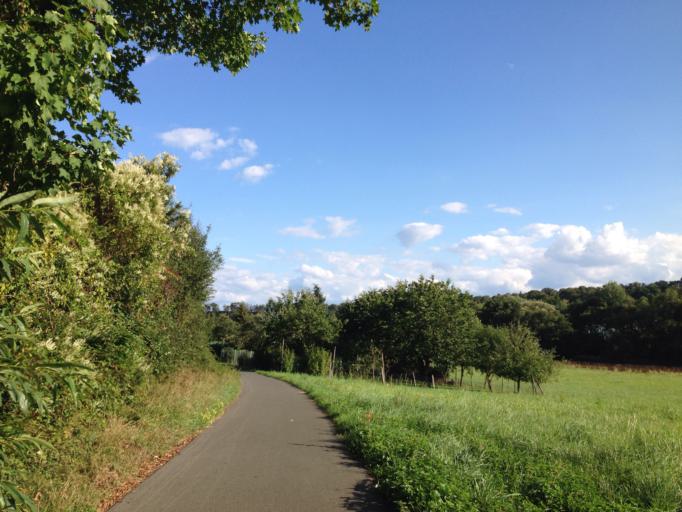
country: DE
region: Hesse
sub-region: Regierungsbezirk Giessen
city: Steeden
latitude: 50.4062
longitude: 8.1311
